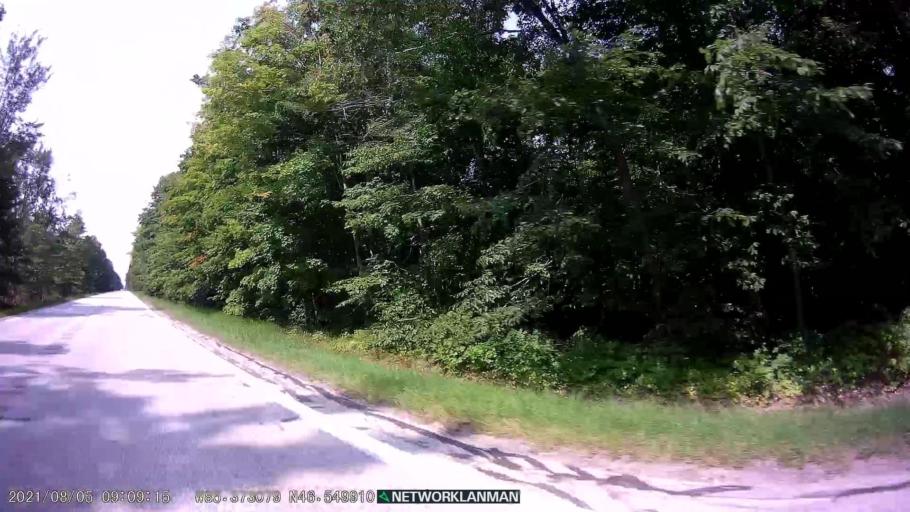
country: US
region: Michigan
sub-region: Luce County
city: Newberry
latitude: 46.5498
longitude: -85.3733
